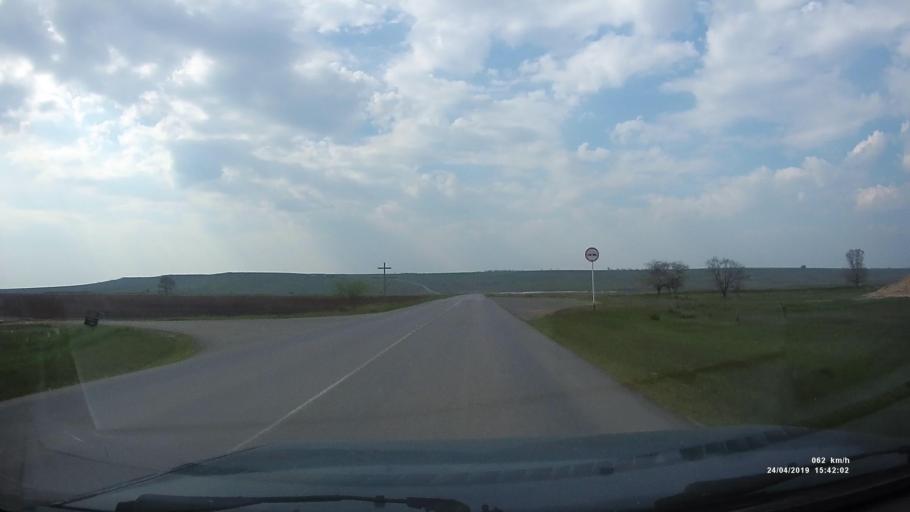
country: RU
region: Kalmykiya
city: Yashalta
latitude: 46.5727
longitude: 42.7922
